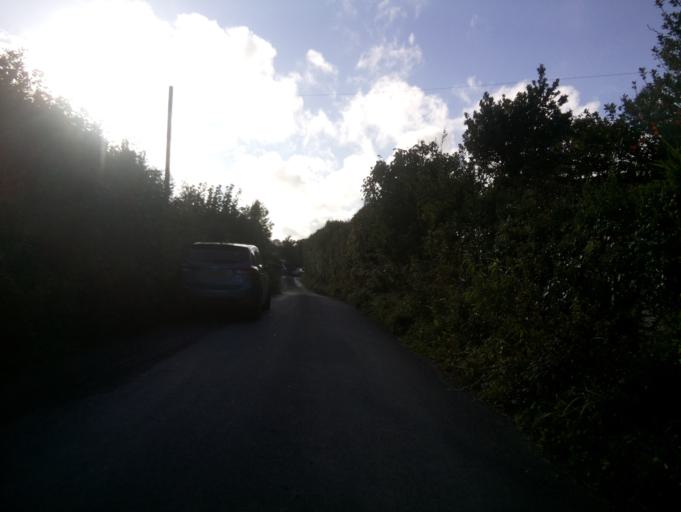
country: GB
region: England
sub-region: Devon
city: Totnes
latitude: 50.3461
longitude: -3.6765
